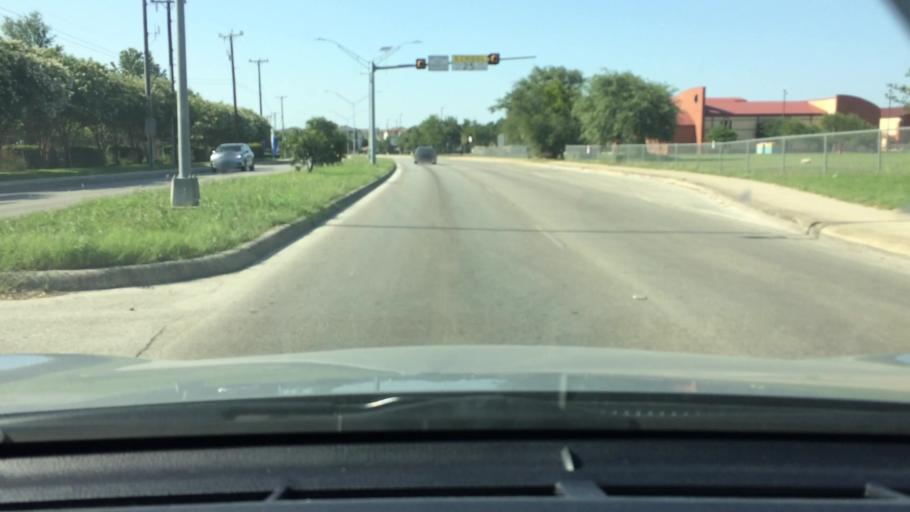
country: US
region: Texas
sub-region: Bexar County
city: Shavano Park
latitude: 29.5741
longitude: -98.5856
